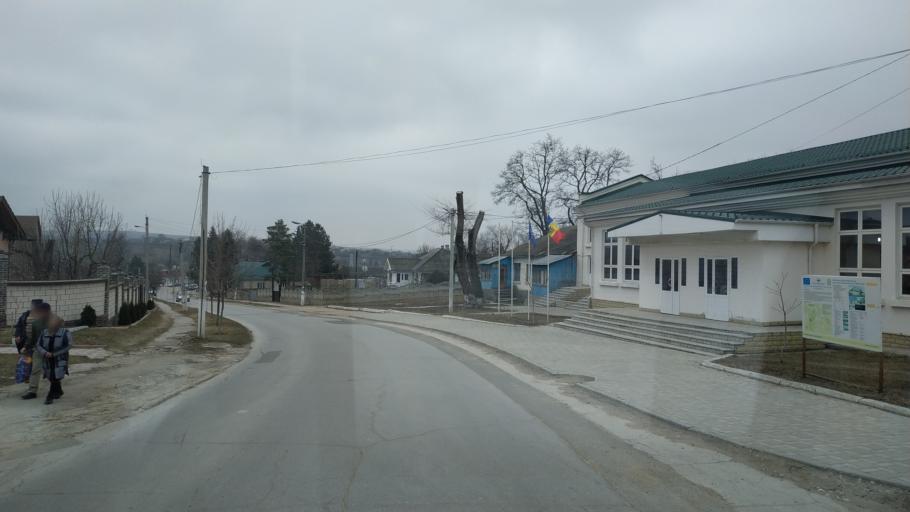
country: MD
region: Hincesti
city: Hincesti
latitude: 46.8843
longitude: 28.4114
